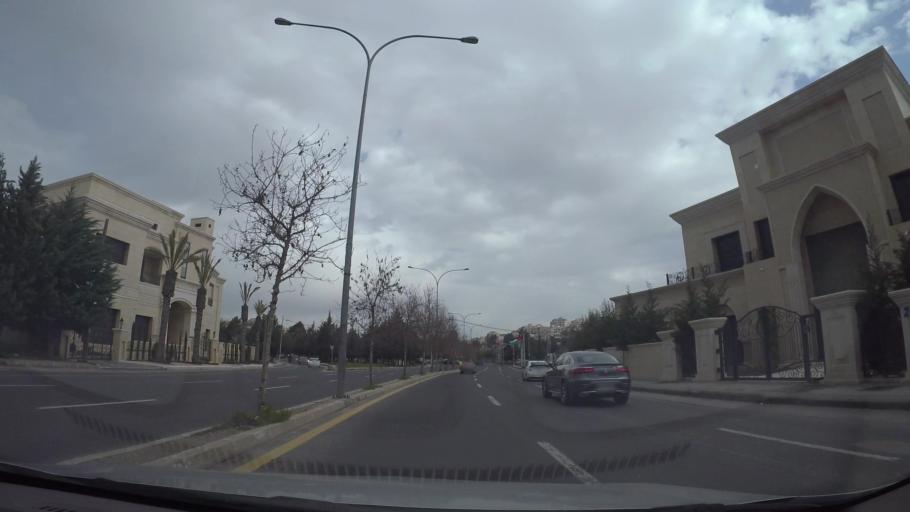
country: JO
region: Amman
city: Wadi as Sir
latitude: 31.9931
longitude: 35.8178
